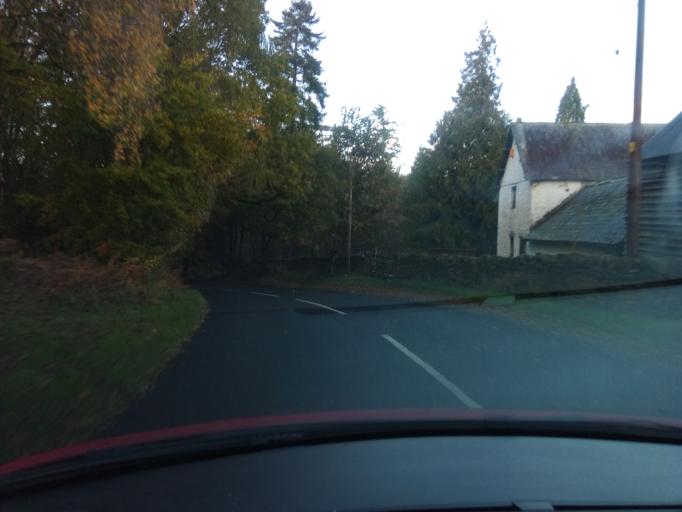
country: GB
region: England
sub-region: County Durham
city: Wolsingham
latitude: 54.6961
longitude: -1.8584
